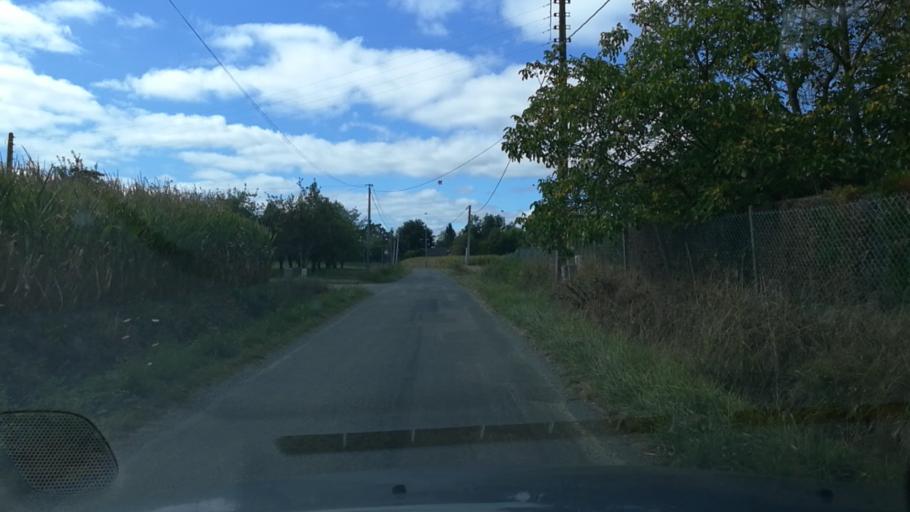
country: FR
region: Brittany
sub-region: Departement d'Ille-et-Vilaine
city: Montgermont
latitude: 48.1464
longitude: -1.7154
